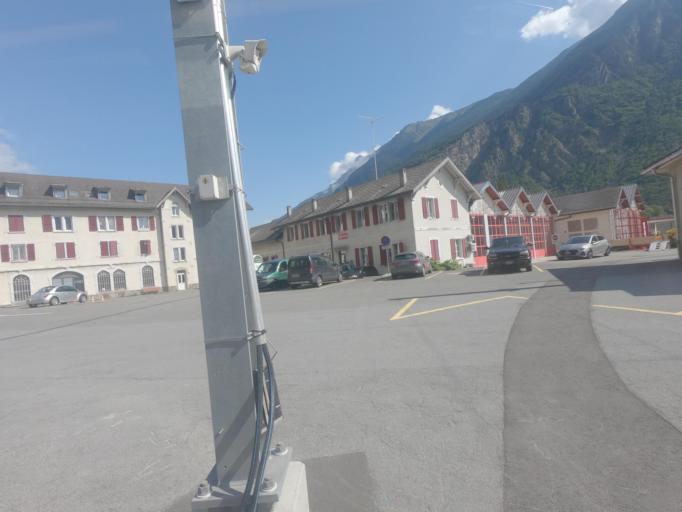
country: CH
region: Valais
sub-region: Saint-Maurice District
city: Vernayaz
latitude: 46.1305
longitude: 7.0445
